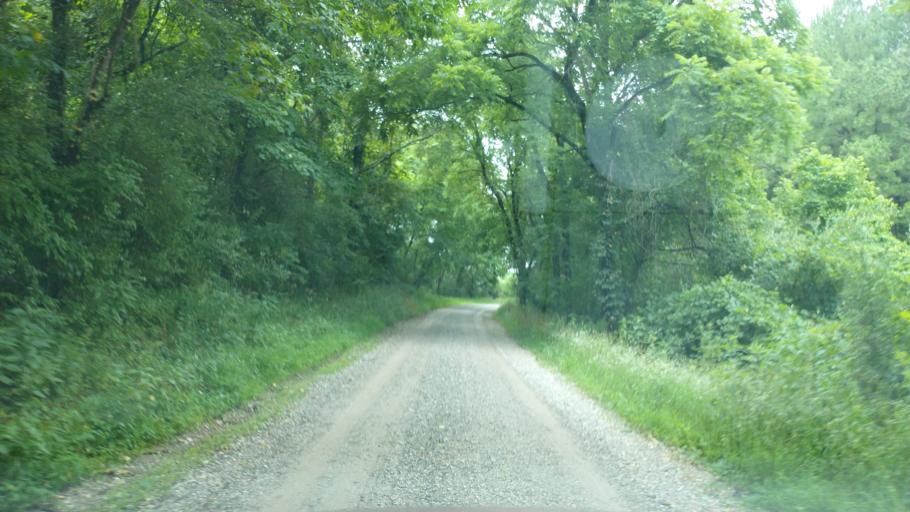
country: US
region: Ohio
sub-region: Meigs County
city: Middleport
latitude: 38.9250
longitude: -82.0540
